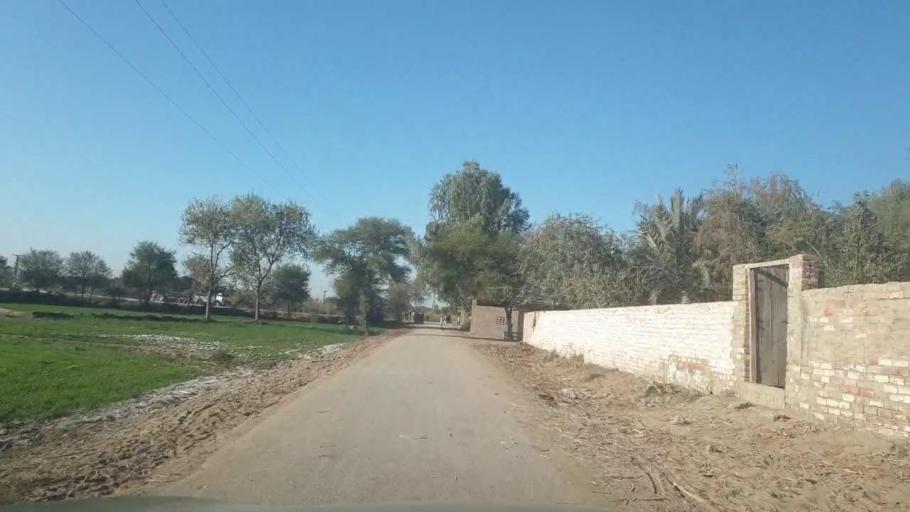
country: PK
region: Sindh
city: Adilpur
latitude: 27.9306
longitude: 69.2554
